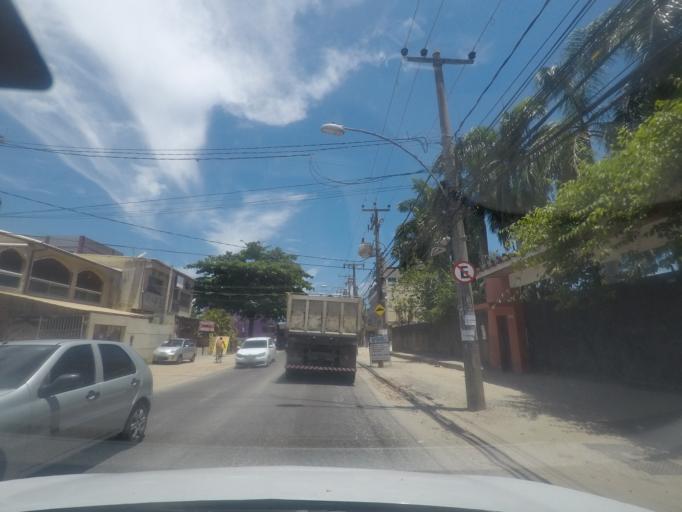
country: BR
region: Rio de Janeiro
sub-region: Itaguai
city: Itaguai
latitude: -22.9361
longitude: -43.6880
